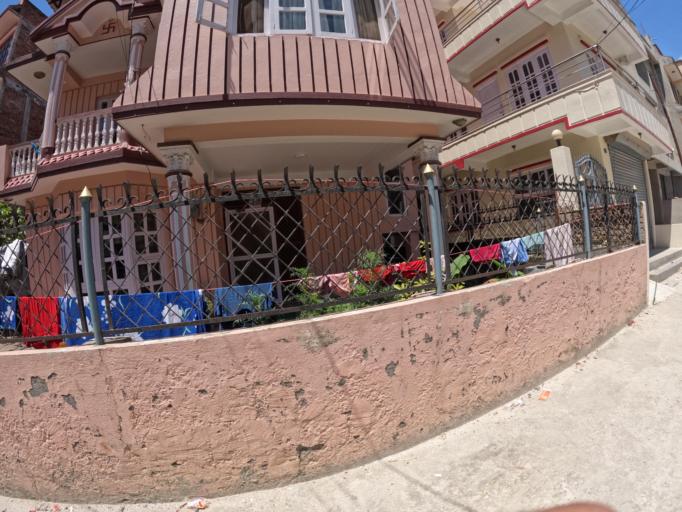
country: NP
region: Central Region
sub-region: Bagmati Zone
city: Kathmandu
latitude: 27.7493
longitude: 85.3275
